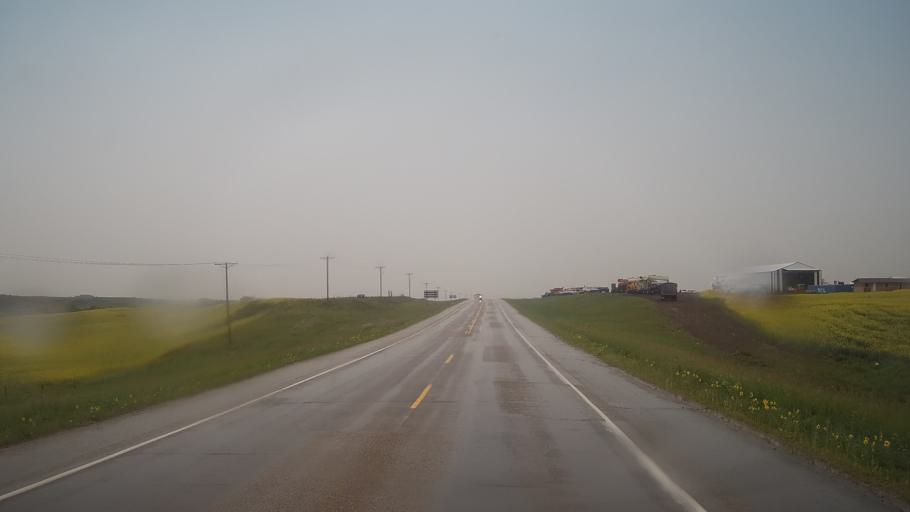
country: CA
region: Saskatchewan
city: Biggar
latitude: 52.0706
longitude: -108.0108
